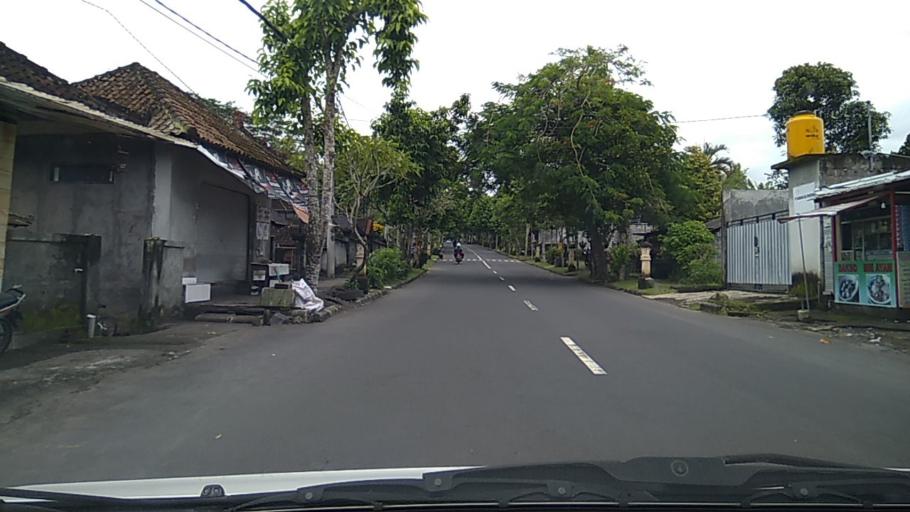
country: ID
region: Bali
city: Banjar Kelodan
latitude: -8.5184
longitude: 115.3459
